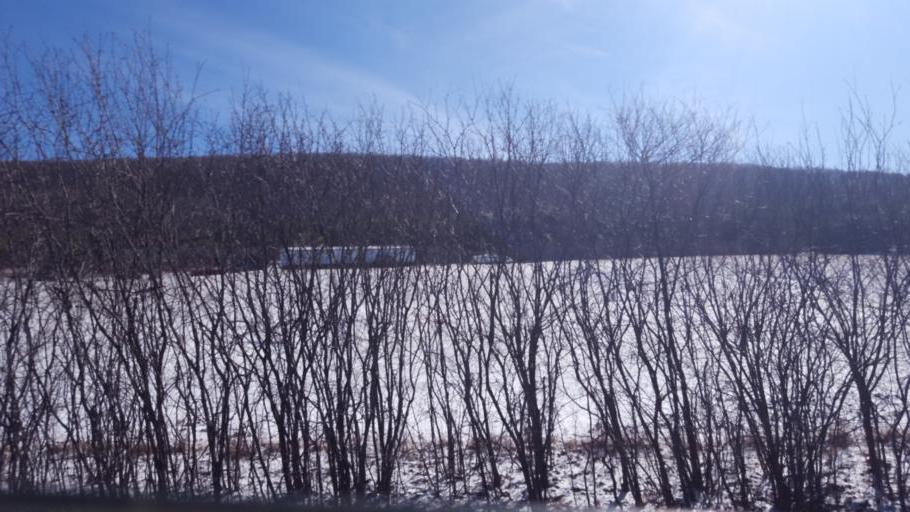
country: US
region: New York
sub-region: Allegany County
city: Wellsville
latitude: 42.1373
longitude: -77.9482
